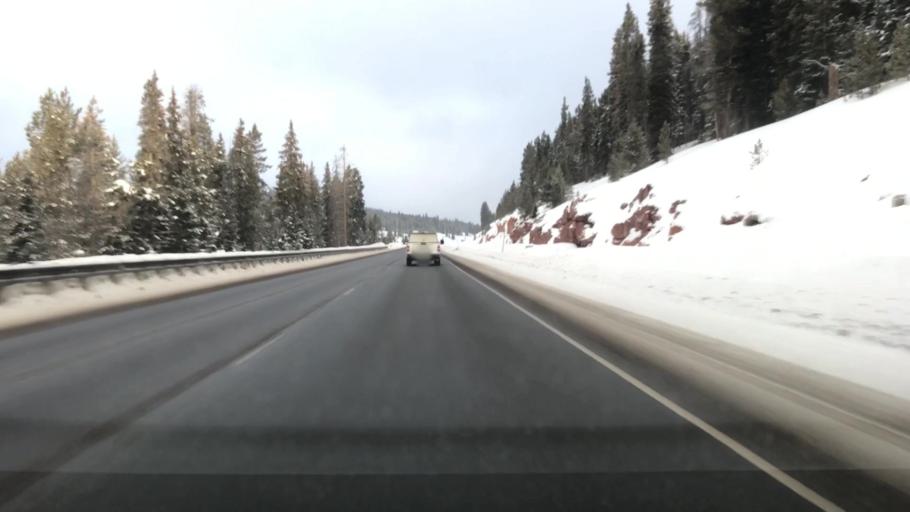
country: US
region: Colorado
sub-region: Summit County
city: Frisco
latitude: 39.5208
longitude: -106.2124
